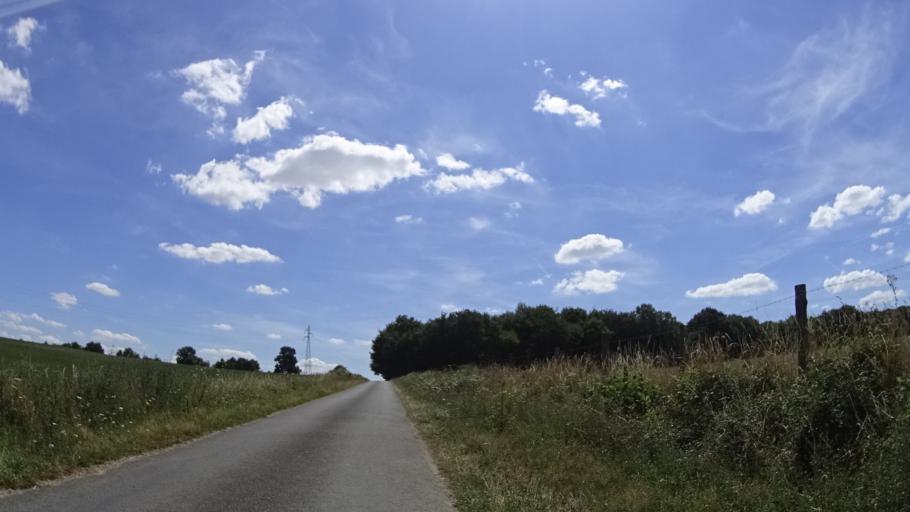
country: FR
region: Pays de la Loire
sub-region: Departement de Maine-et-Loire
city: Cande
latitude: 47.6130
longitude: -1.0131
